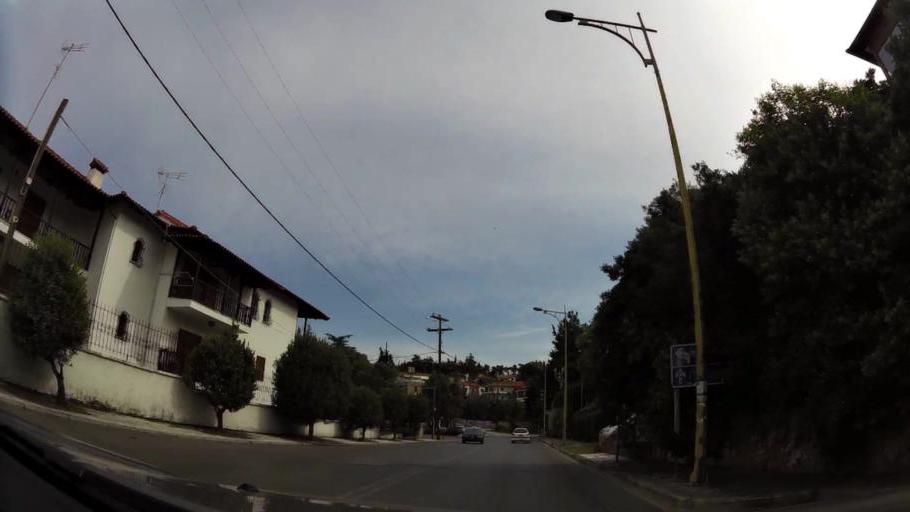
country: GR
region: Central Macedonia
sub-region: Nomos Thessalonikis
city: Panorama
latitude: 40.5902
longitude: 23.0197
